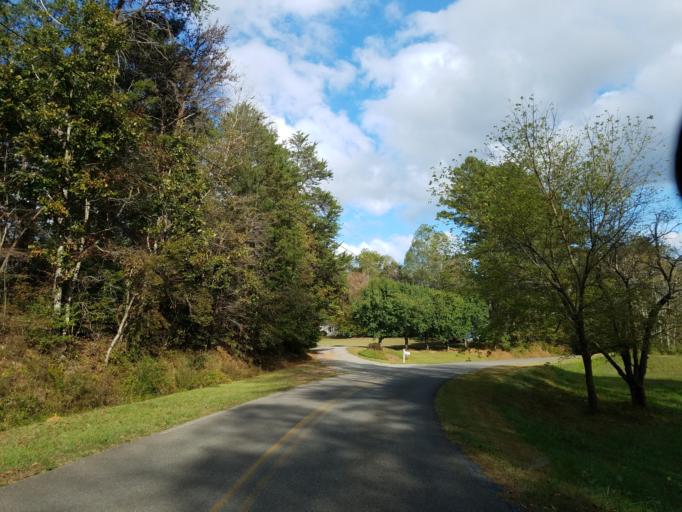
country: US
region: Georgia
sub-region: Gilmer County
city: Ellijay
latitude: 34.6443
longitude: -84.3470
